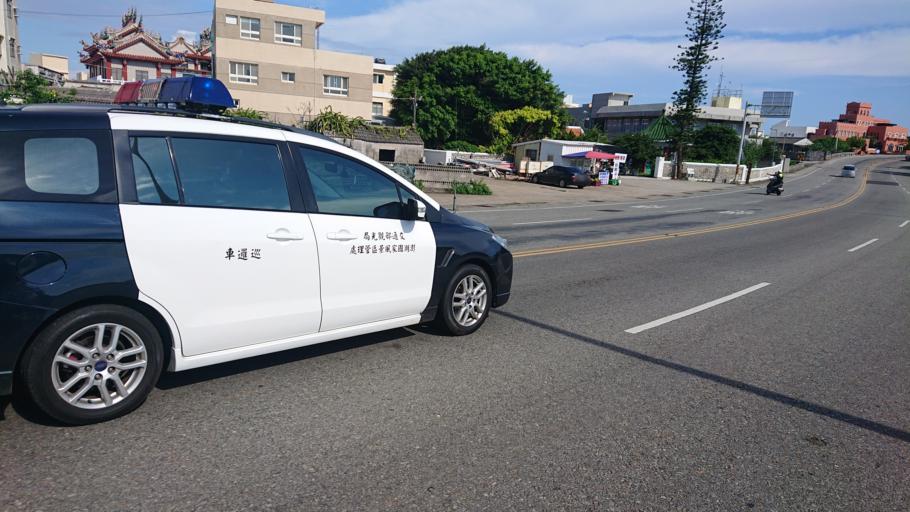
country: TW
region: Taiwan
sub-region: Penghu
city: Ma-kung
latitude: 23.5513
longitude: 119.6104
